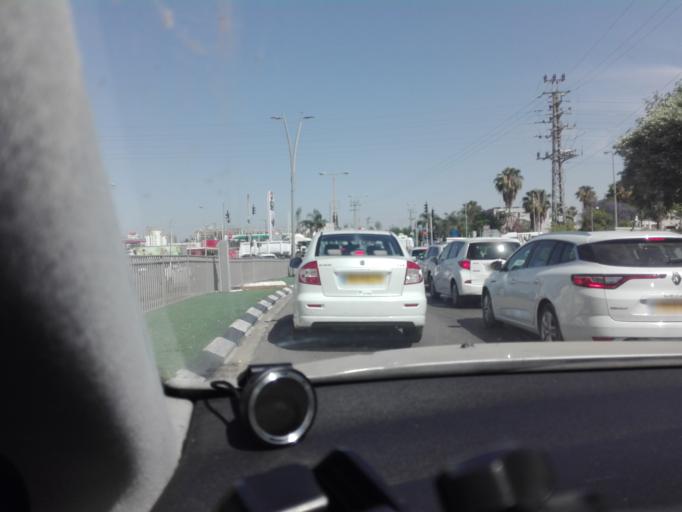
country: IL
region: Central District
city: Bene 'Ayish
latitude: 31.7278
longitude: 34.7489
